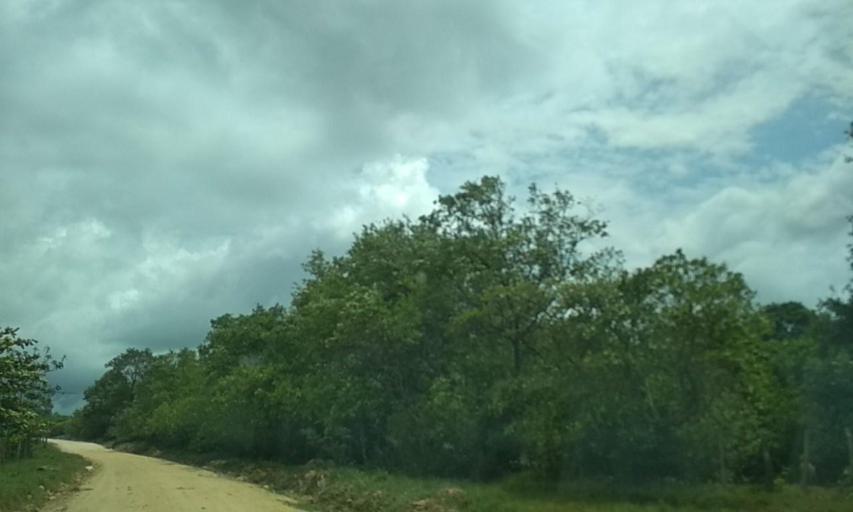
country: MX
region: Veracruz
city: Las Choapas
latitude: 17.9056
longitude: -94.1254
